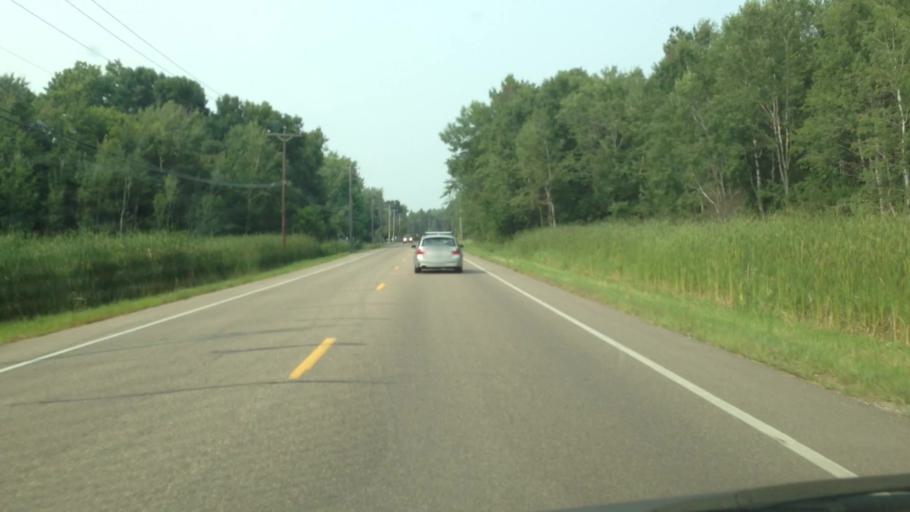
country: US
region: Minnesota
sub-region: Anoka County
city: Circle Pines
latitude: 45.1324
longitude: -93.1273
